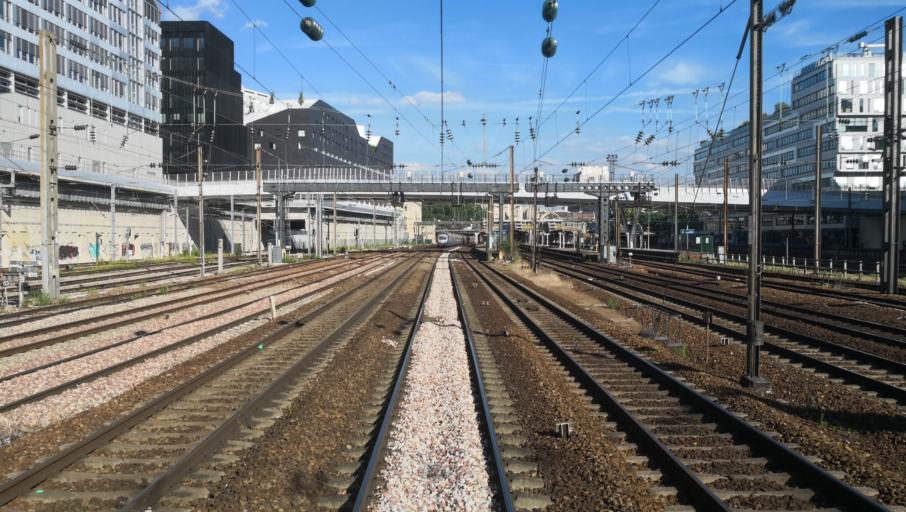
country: FR
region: Ile-de-France
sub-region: Paris
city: Saint-Ouen
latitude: 48.8852
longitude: 2.3249
